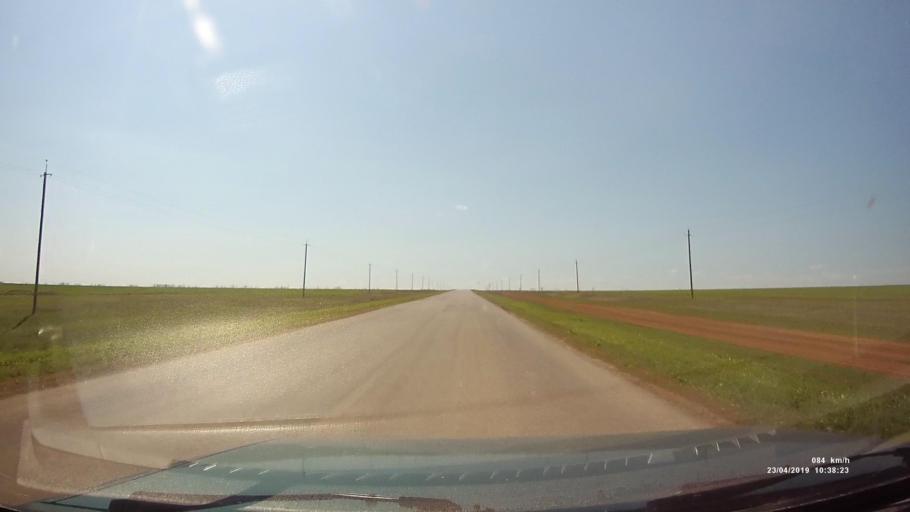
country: RU
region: Kalmykiya
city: Yashalta
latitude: 46.5333
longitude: 42.6388
